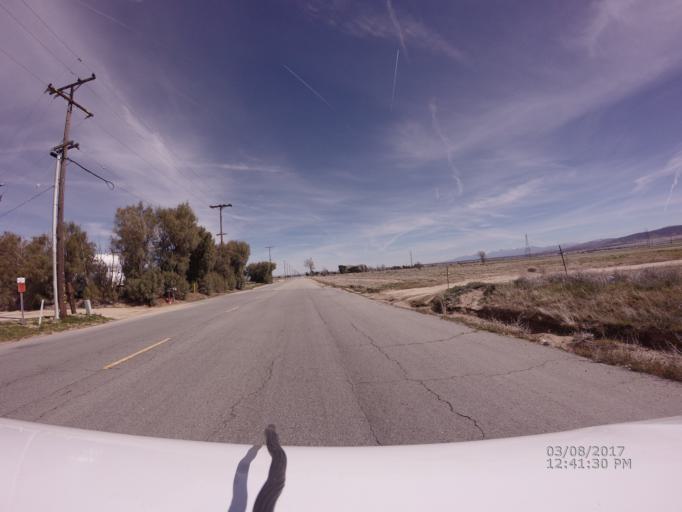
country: US
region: California
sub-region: Los Angeles County
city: Leona Valley
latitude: 34.7038
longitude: -118.3027
